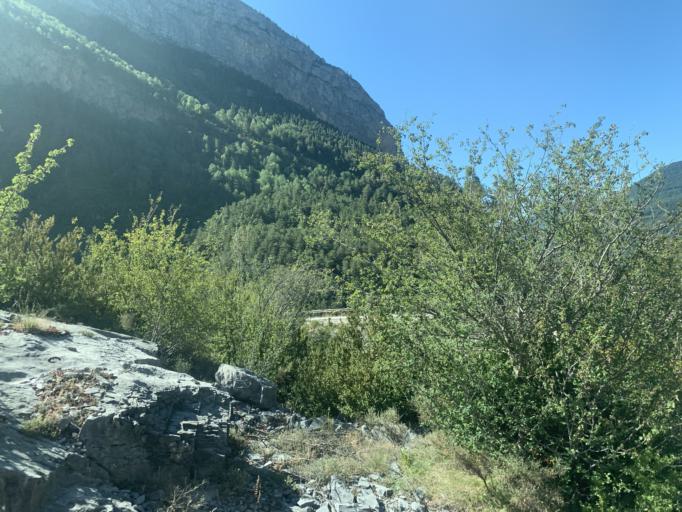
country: ES
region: Aragon
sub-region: Provincia de Huesca
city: Broto
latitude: 42.6530
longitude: -0.1004
